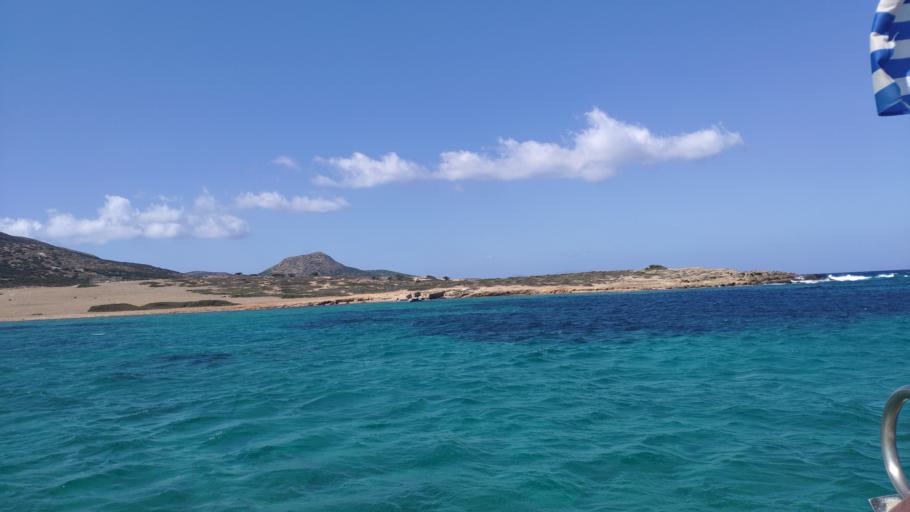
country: GR
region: South Aegean
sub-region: Nomos Kykladon
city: Antiparos
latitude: 36.9733
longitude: 25.0190
